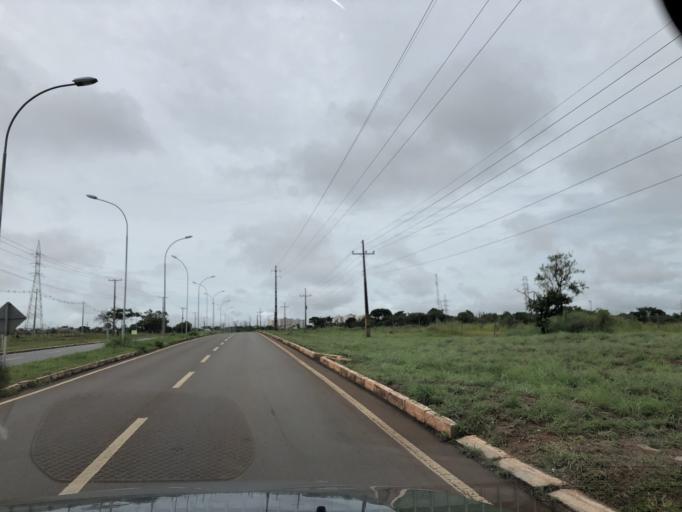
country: BR
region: Federal District
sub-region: Brasilia
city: Brasilia
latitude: -15.7774
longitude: -48.1294
